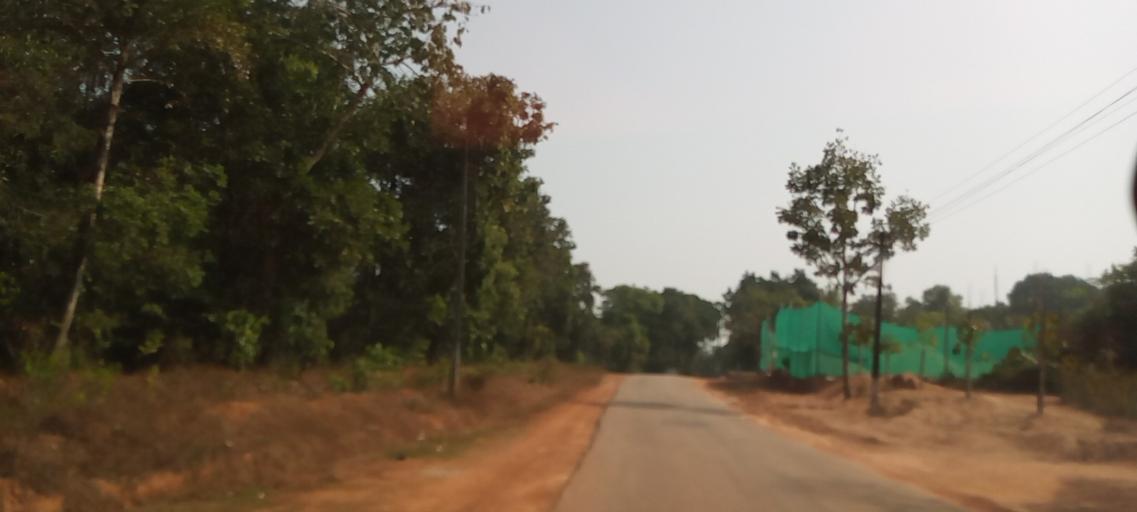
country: IN
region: Karnataka
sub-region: Udupi
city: Manipala
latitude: 13.5130
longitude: 74.8410
